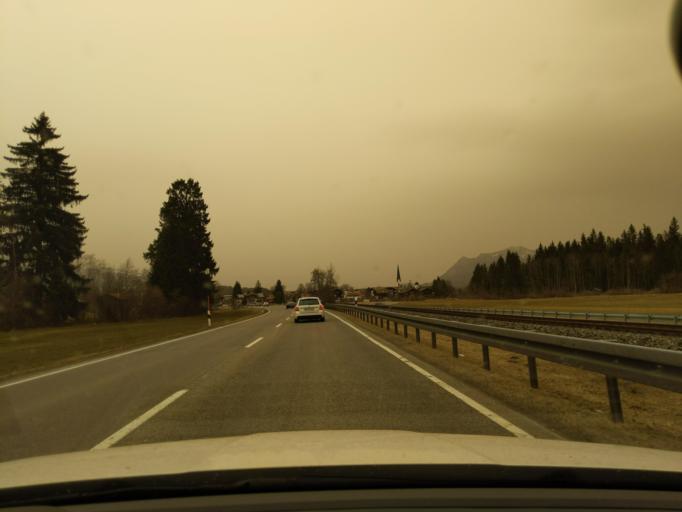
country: DE
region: Bavaria
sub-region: Swabia
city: Obermaiselstein
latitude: 47.4515
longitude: 10.2724
